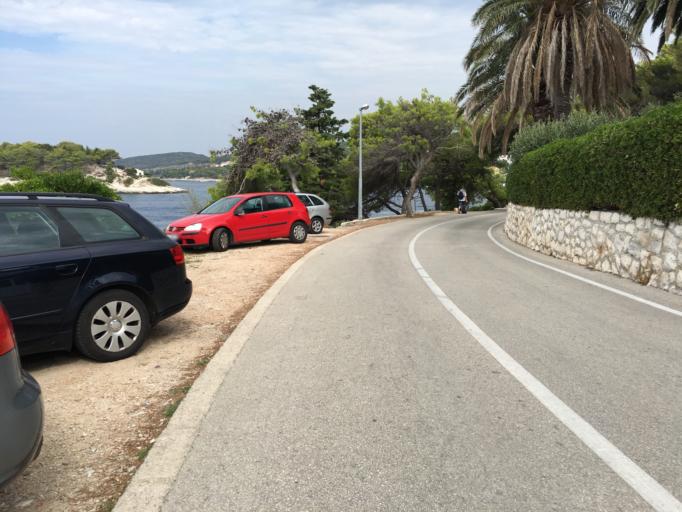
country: HR
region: Splitsko-Dalmatinska
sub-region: Grad Hvar
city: Hvar
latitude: 43.1644
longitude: 16.4417
